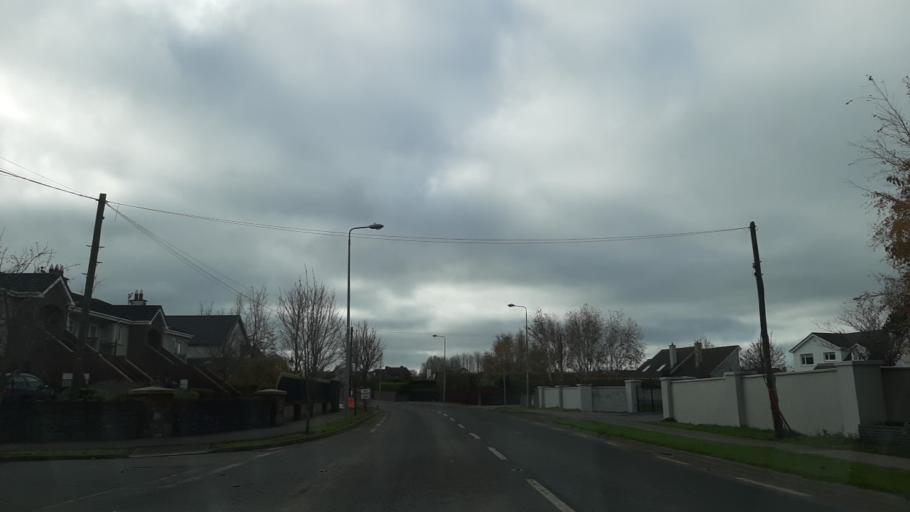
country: IE
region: Leinster
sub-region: Kildare
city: Kildare
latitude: 53.1681
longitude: -6.9030
